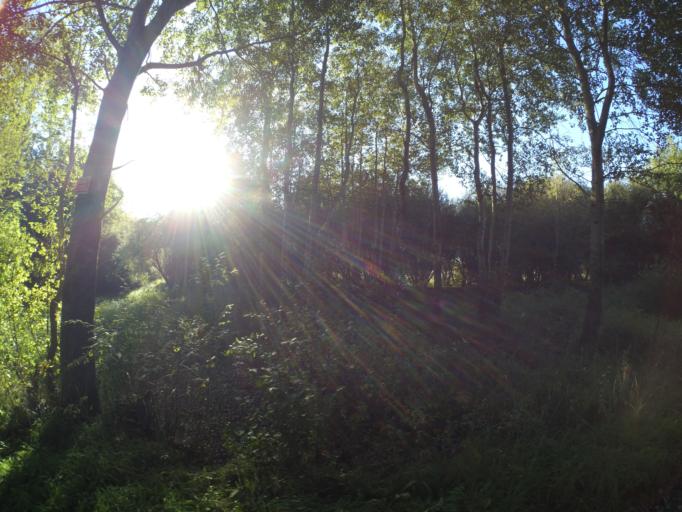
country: FR
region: Brittany
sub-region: Departement du Morbihan
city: Saint-Vincent-sur-Oust
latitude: 47.7188
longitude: -2.1476
